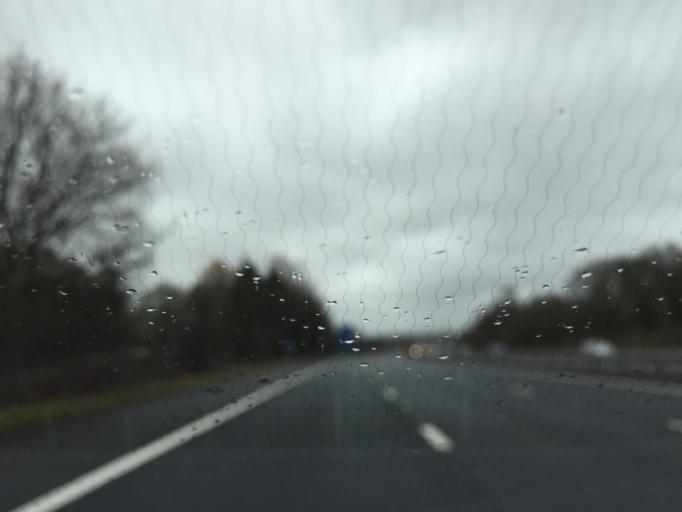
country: GB
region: England
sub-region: Hampshire
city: Cadnam
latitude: 50.9442
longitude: -1.5419
